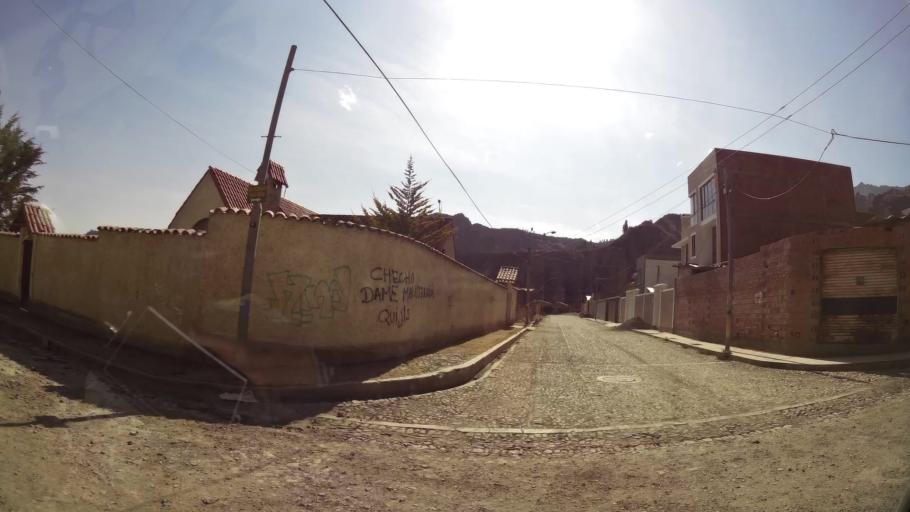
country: BO
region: La Paz
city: La Paz
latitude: -16.5086
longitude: -68.0523
